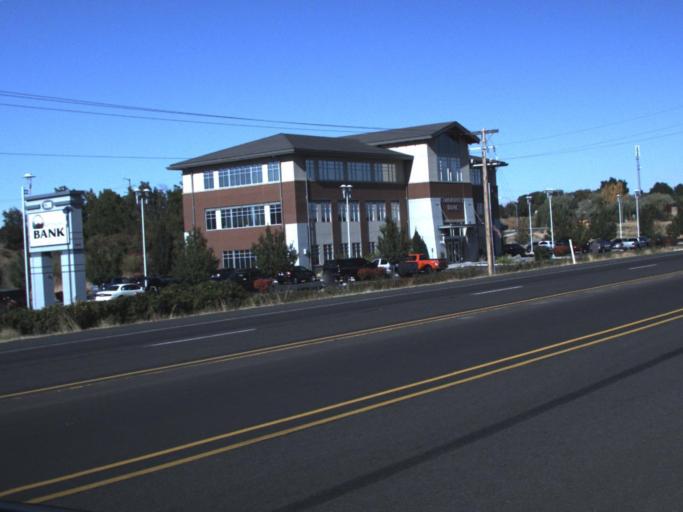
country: US
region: Washington
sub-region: Walla Walla County
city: College Place
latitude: 46.0403
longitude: -118.3649
